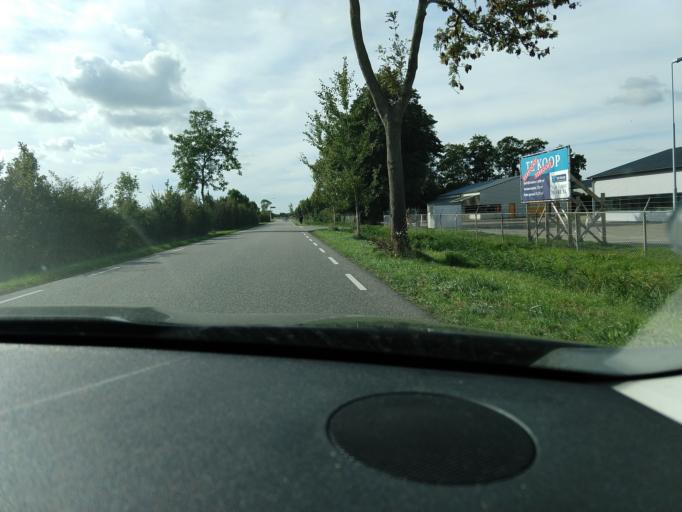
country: NL
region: Zeeland
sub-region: Gemeente Middelburg
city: Middelburg
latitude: 51.5424
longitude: 3.5963
